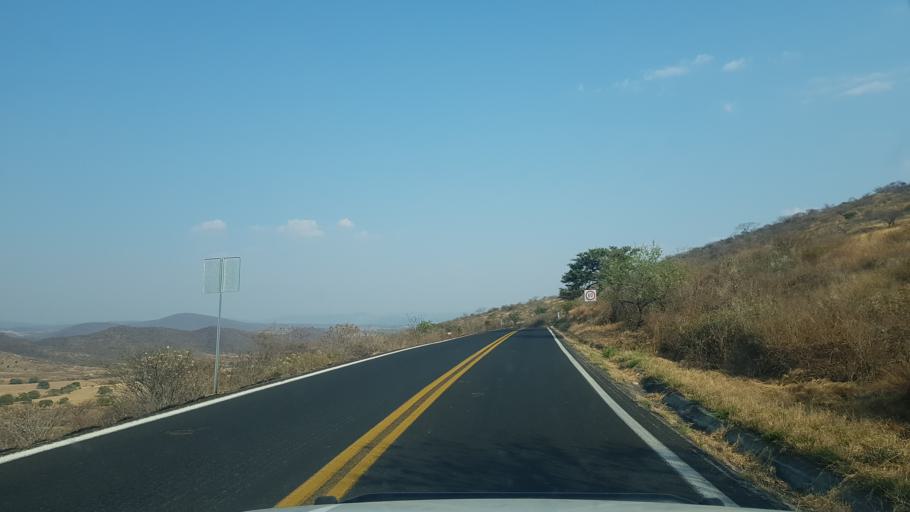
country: MX
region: Puebla
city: Calmeca
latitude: 18.6458
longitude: -98.5988
